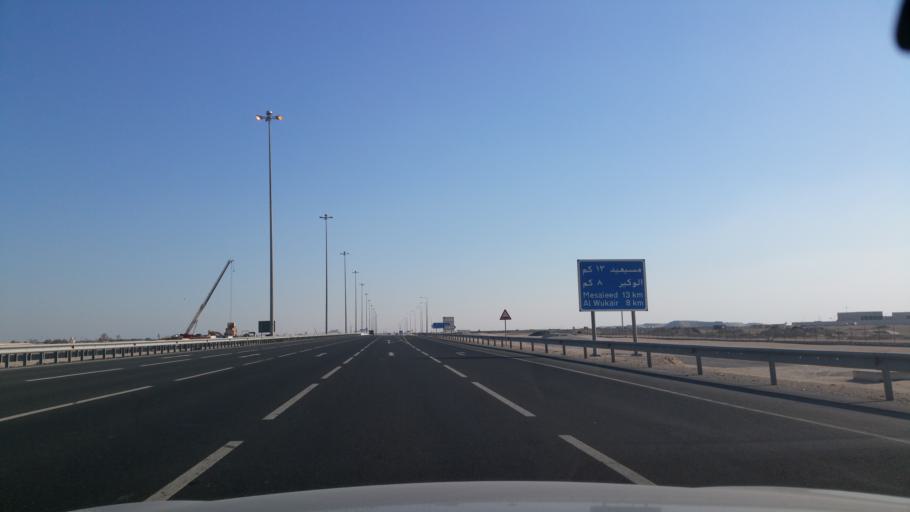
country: QA
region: Al Wakrah
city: Al Wukayr
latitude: 25.1560
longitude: 51.4732
